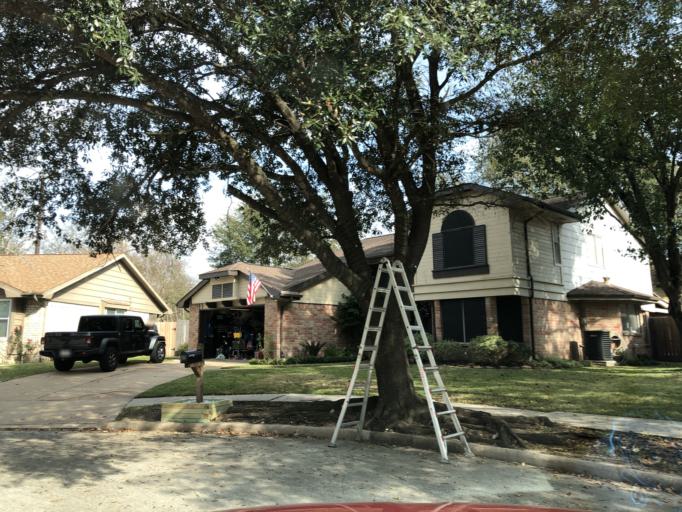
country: US
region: Texas
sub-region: Harris County
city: Tomball
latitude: 30.0377
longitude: -95.5418
